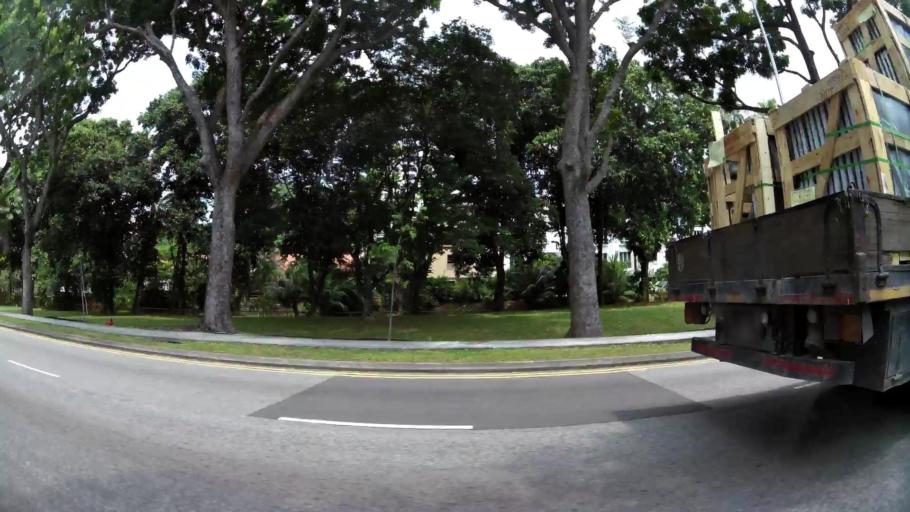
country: SG
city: Singapore
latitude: 1.2858
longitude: 103.7794
